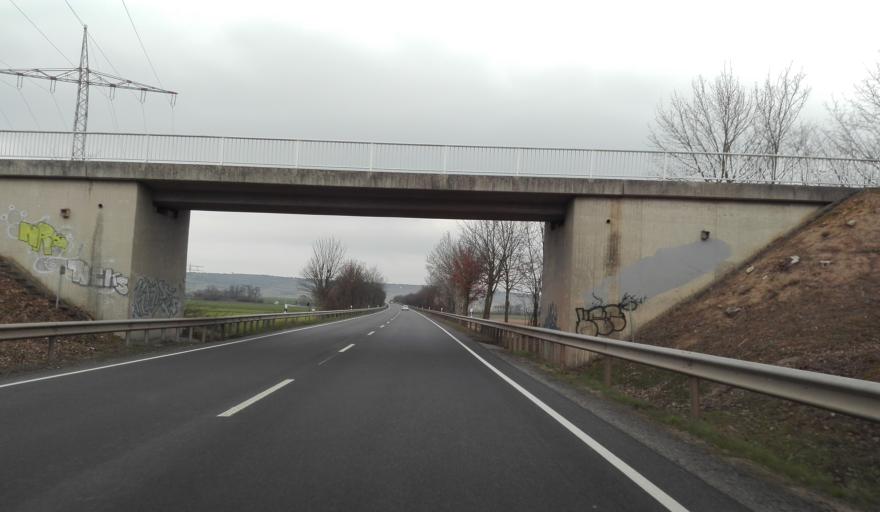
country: DE
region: Rheinland-Pfalz
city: Heidesheim
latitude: 49.5695
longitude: 8.1847
